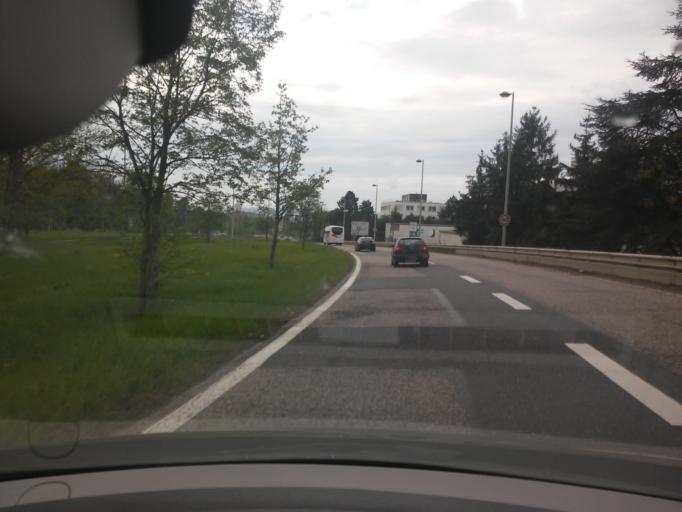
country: FR
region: Lorraine
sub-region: Departement de Meurthe-et-Moselle
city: Laxou
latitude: 48.7035
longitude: 6.1347
